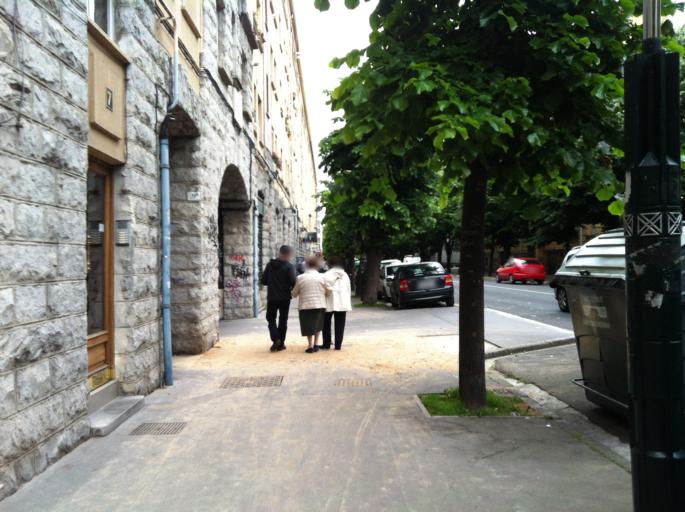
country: ES
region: Basque Country
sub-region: Provincia de Alava
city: Gasteiz / Vitoria
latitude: 42.8384
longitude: -2.6694
